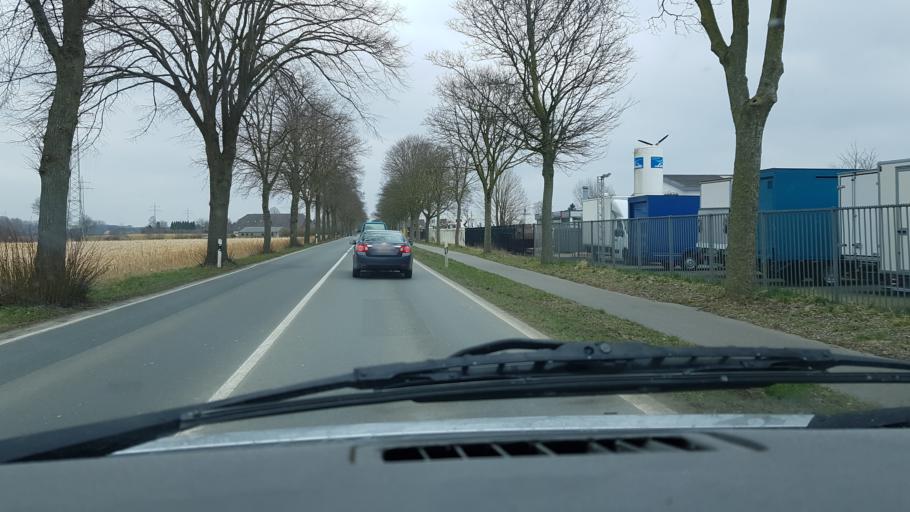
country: DE
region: North Rhine-Westphalia
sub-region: Regierungsbezirk Dusseldorf
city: Kranenburg
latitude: 51.7849
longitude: 6.0494
